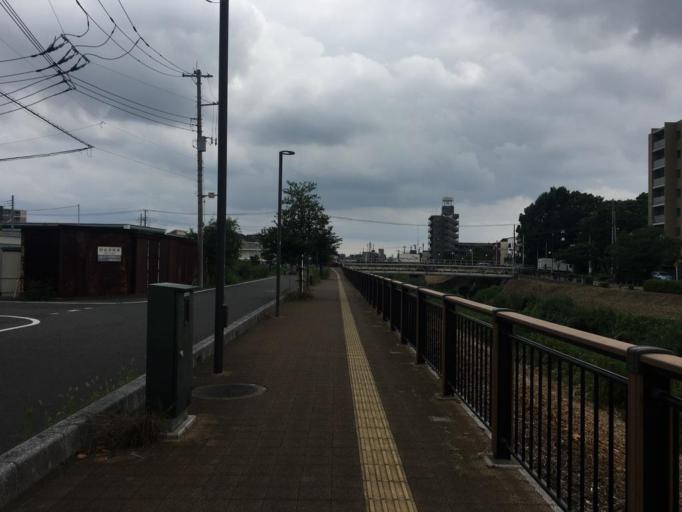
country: JP
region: Saitama
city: Shimotoda
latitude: 35.8235
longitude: 139.6590
